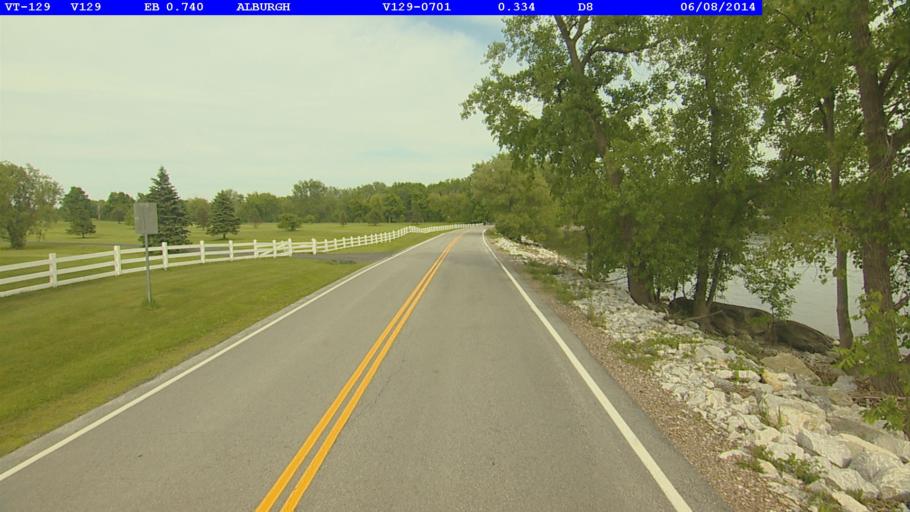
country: US
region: Vermont
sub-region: Grand Isle County
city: North Hero
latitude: 44.9042
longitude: -73.3096
